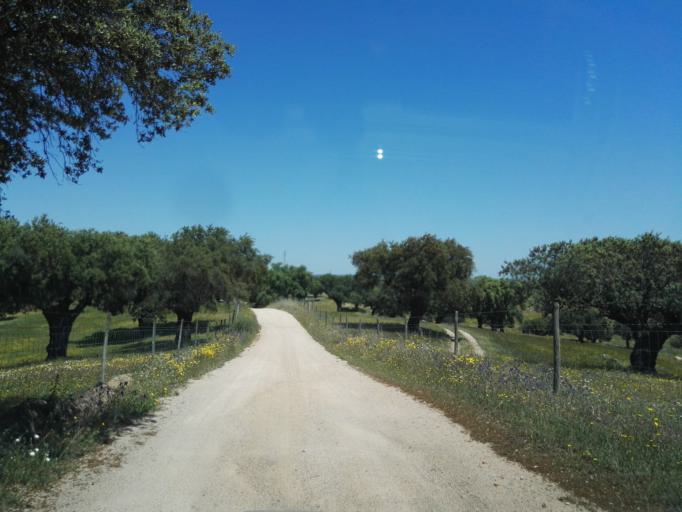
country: PT
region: Portalegre
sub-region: Campo Maior
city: Campo Maior
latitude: 38.9995
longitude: -7.1749
